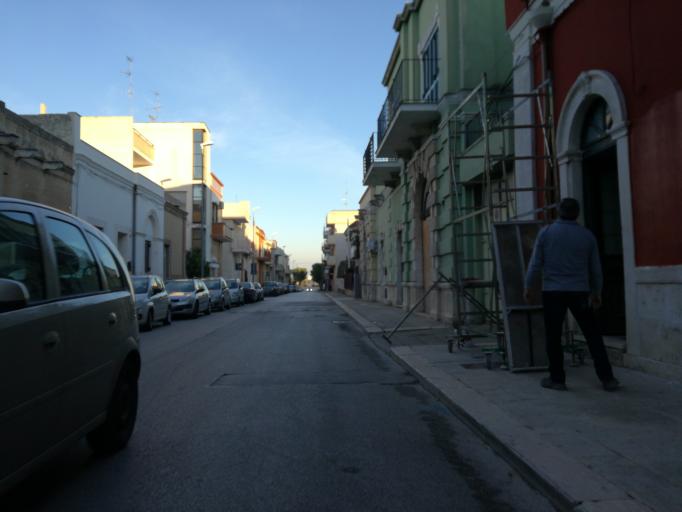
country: IT
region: Apulia
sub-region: Provincia di Bari
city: Adelfia
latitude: 41.0040
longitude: 16.8791
